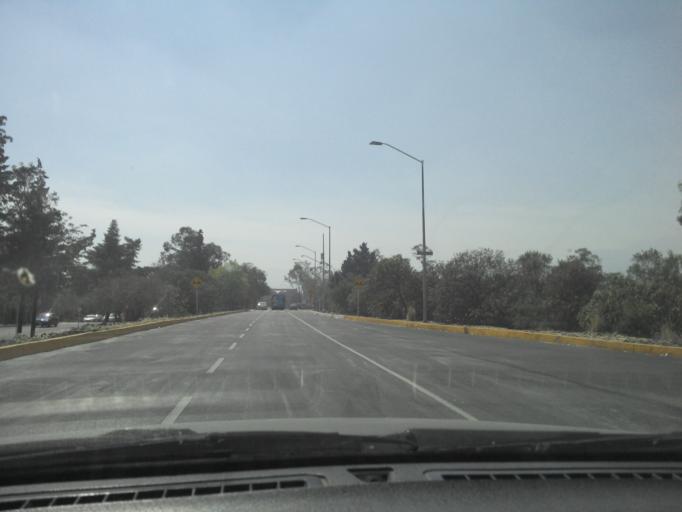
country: MX
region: Mexico City
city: Tlalpan
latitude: 19.3166
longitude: -99.1864
